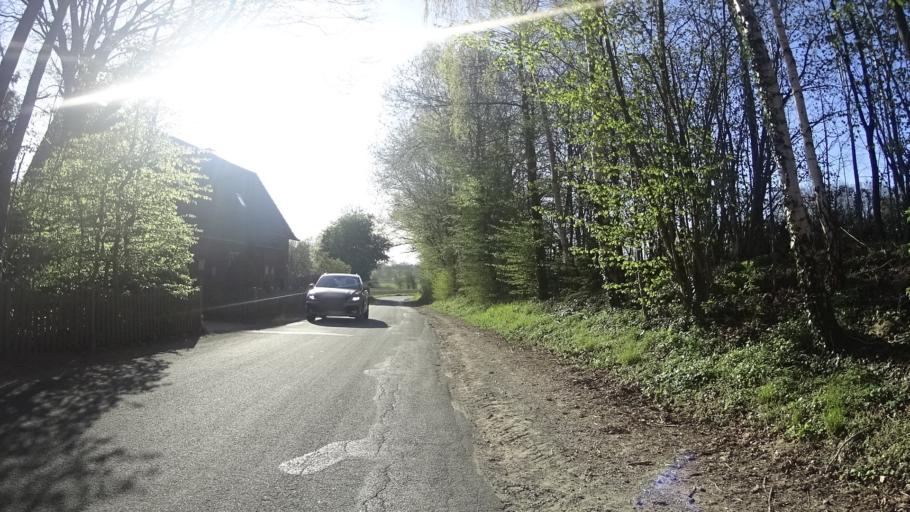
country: DE
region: North Rhine-Westphalia
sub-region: Regierungsbezirk Munster
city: Greven
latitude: 52.0759
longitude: 7.6060
